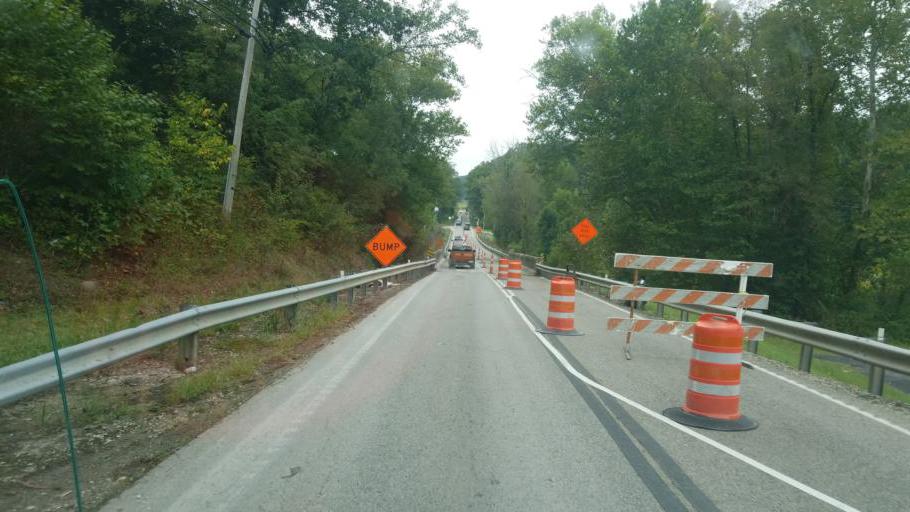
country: US
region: Kentucky
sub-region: Rowan County
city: Morehead
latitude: 38.2111
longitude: -83.4700
